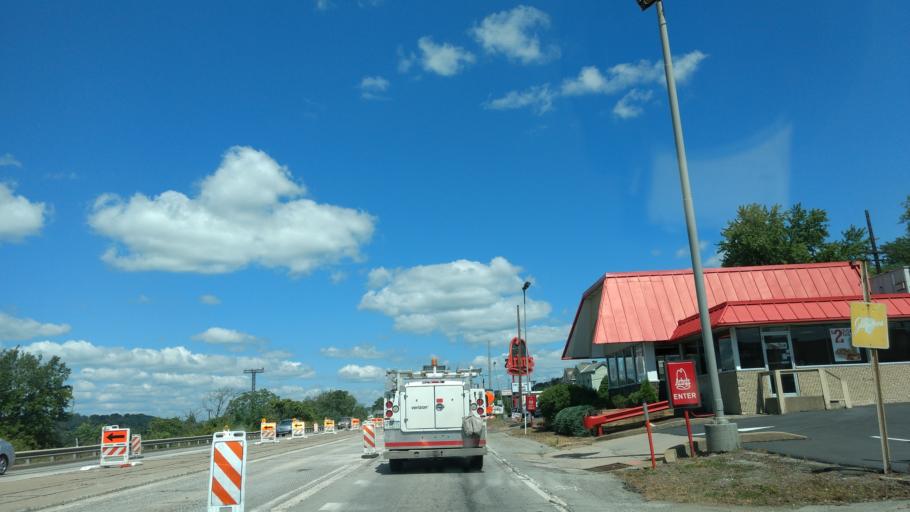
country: US
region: Pennsylvania
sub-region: Beaver County
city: Conway
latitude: 40.6576
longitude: -80.2383
